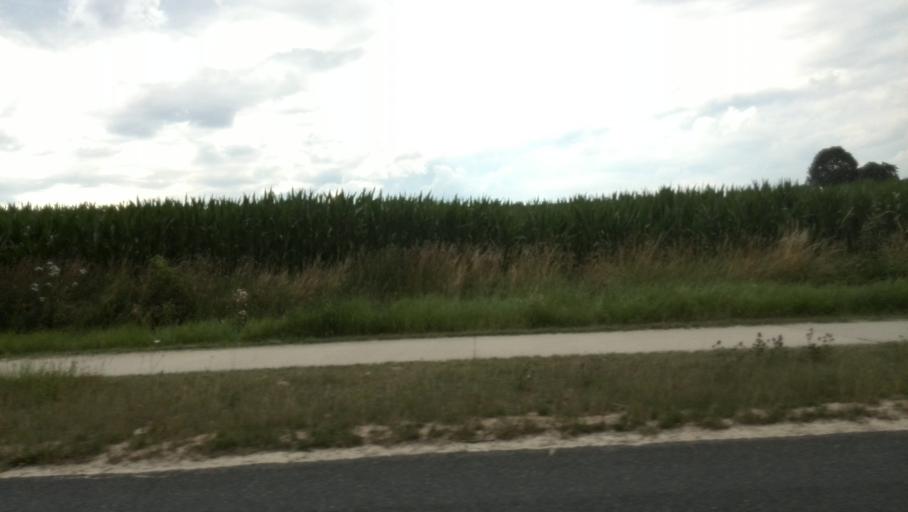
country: DE
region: Lower Saxony
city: Haverlah
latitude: 52.0766
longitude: 10.1726
